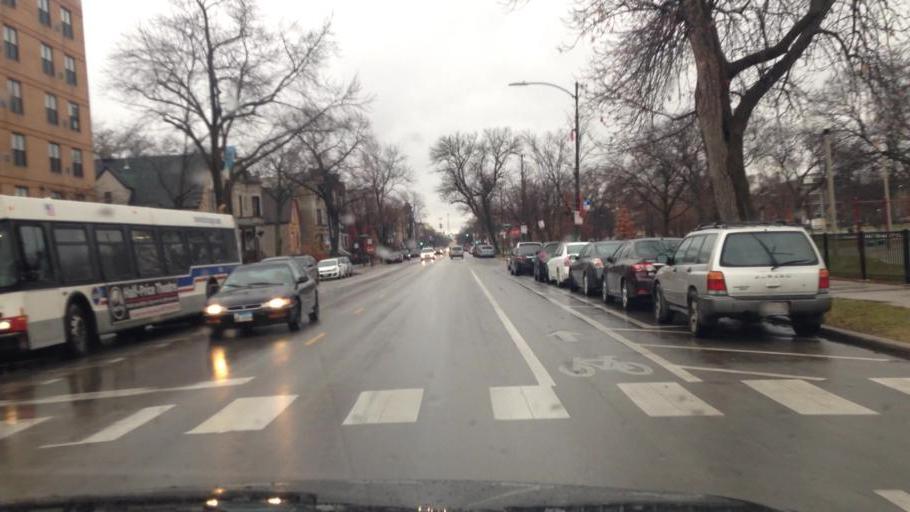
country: US
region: Illinois
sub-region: Cook County
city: Chicago
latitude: 41.9057
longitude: -87.6970
